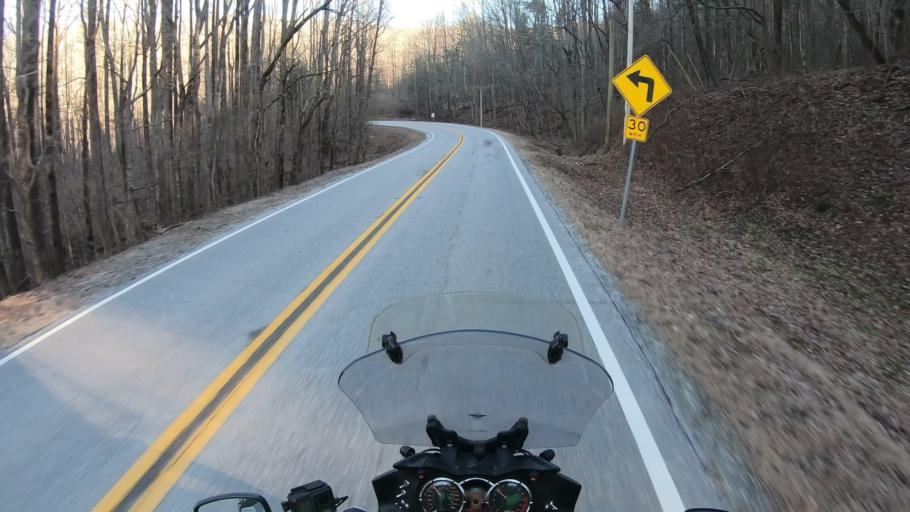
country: US
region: Georgia
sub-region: Lumpkin County
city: Dahlonega
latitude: 34.6894
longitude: -84.0155
